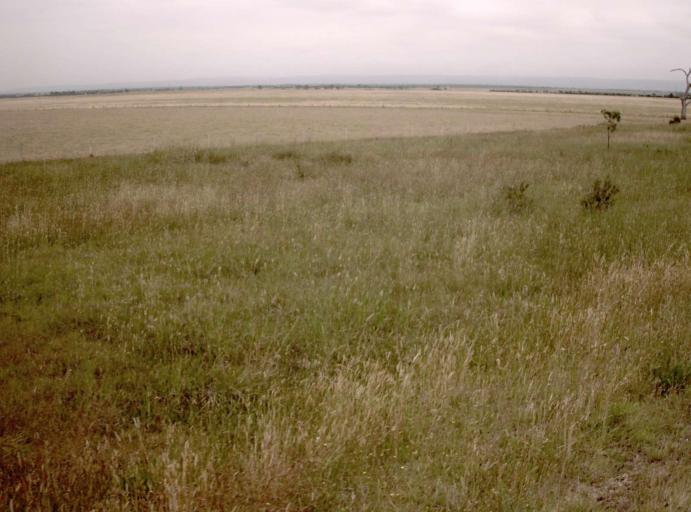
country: AU
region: Victoria
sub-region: Wellington
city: Heyfield
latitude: -38.1232
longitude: 146.7817
